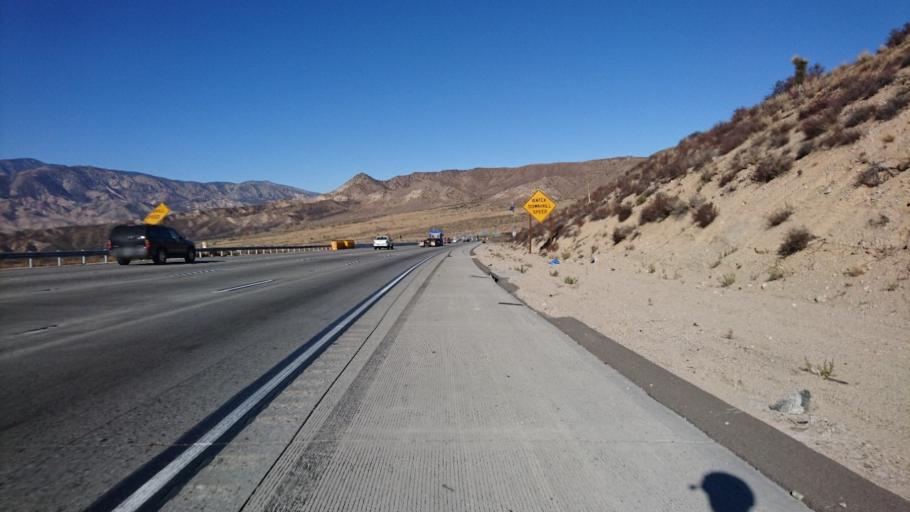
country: US
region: California
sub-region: San Bernardino County
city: Oak Hills
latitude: 34.3452
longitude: -117.4644
